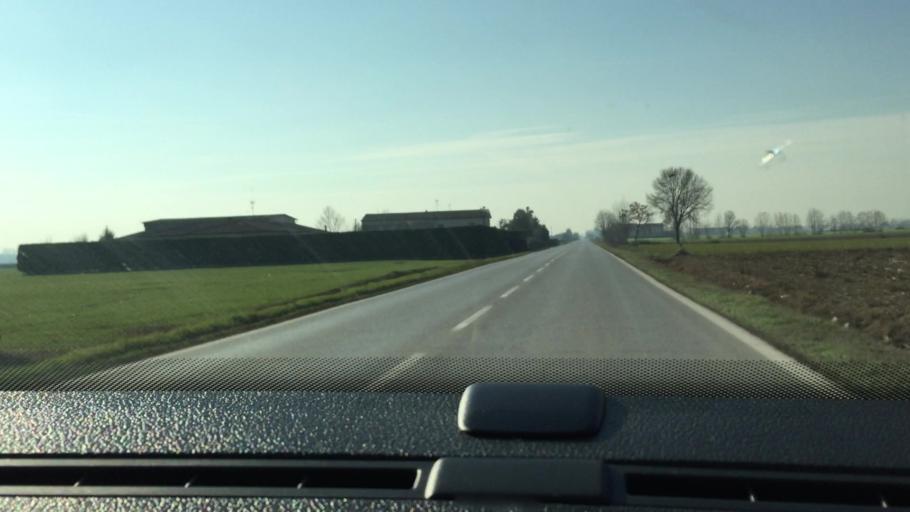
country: IT
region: Lombardy
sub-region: Provincia di Mantova
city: Goito
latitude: 45.2323
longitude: 10.6347
